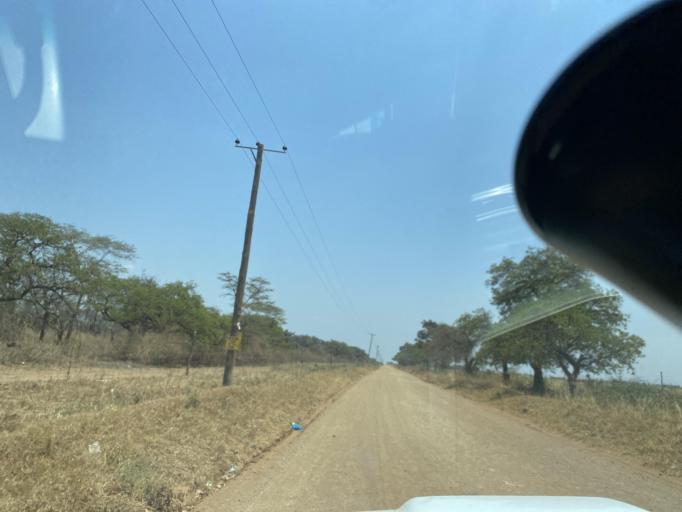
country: ZM
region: Lusaka
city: Lusaka
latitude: -15.4339
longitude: 28.0799
